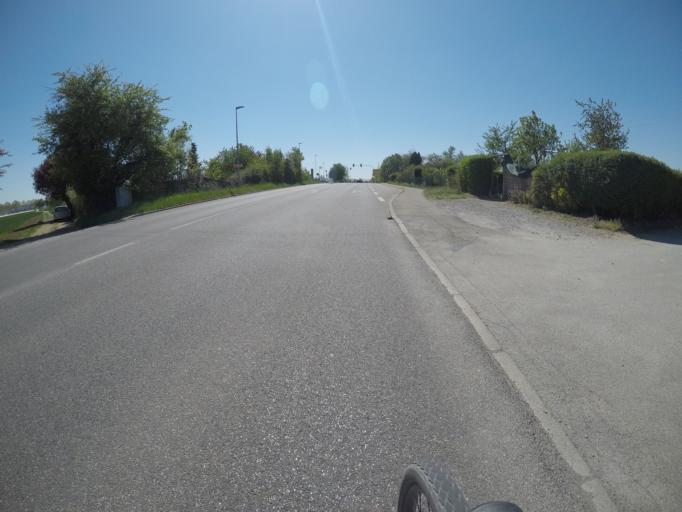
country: DE
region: Baden-Wuerttemberg
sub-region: Regierungsbezirk Stuttgart
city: Stuttgart Muehlhausen
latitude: 48.8278
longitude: 9.2544
